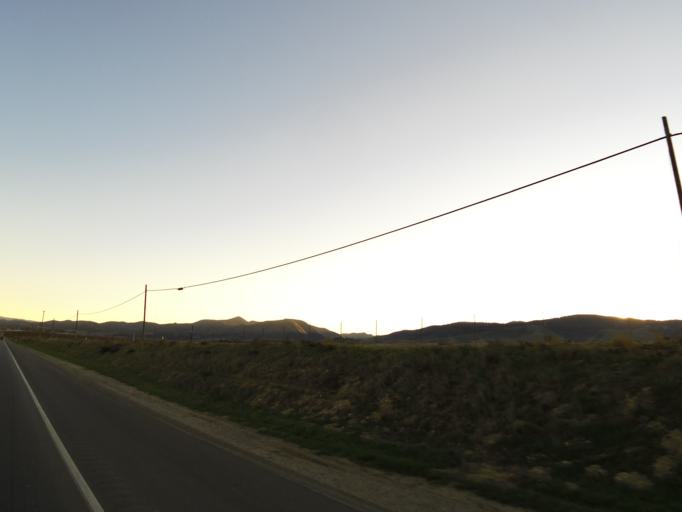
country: US
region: California
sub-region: Monterey County
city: King City
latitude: 36.2610
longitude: -121.1793
